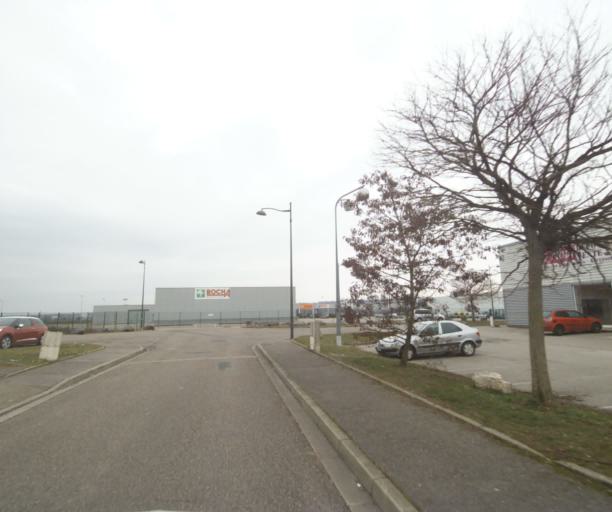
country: FR
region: Champagne-Ardenne
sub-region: Departement de la Haute-Marne
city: Saint-Dizier
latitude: 48.6255
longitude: 4.9702
